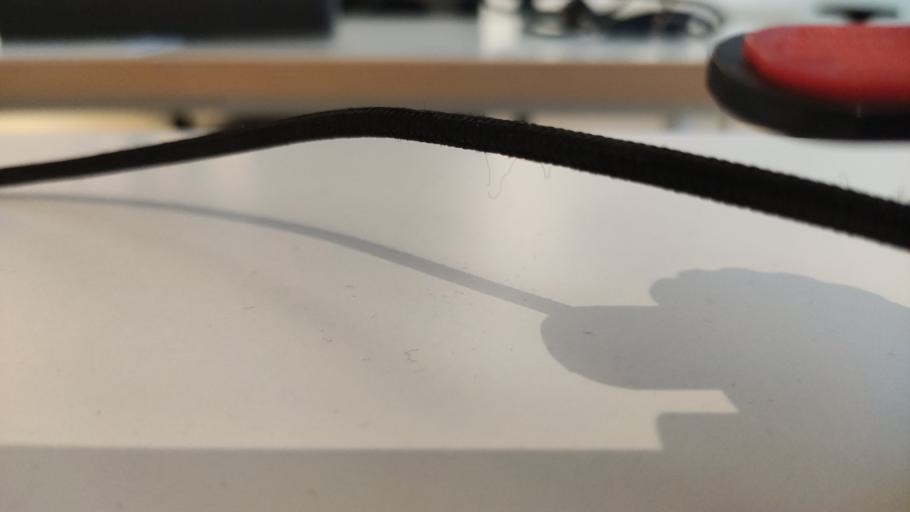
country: RU
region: Moskovskaya
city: Sychevo
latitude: 55.8331
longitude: 36.3245
